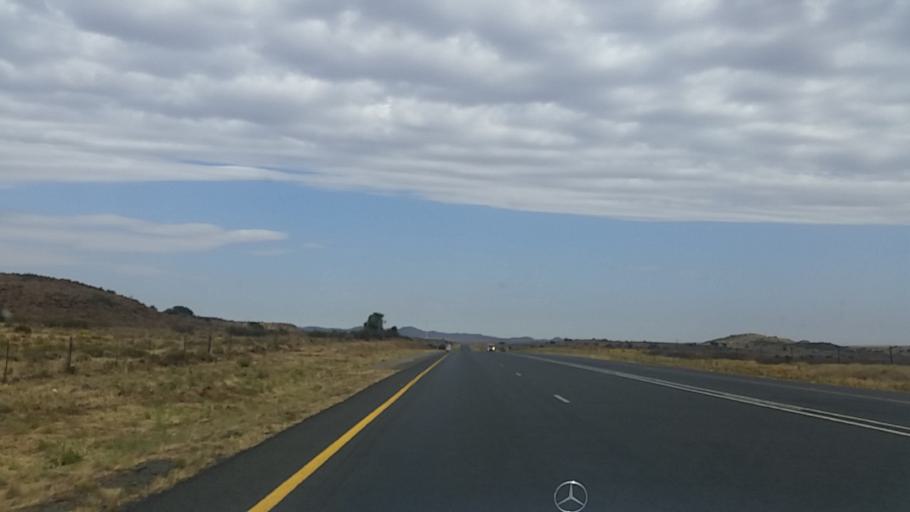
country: ZA
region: Northern Cape
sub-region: Pixley ka Seme District Municipality
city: Colesberg
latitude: -30.6193
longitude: 25.3268
